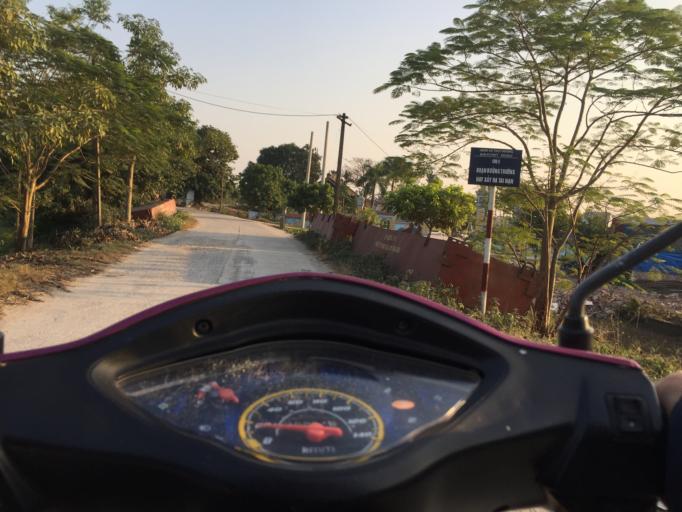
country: VN
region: Ha Noi
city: Chuc Son
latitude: 20.9097
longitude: 105.7137
